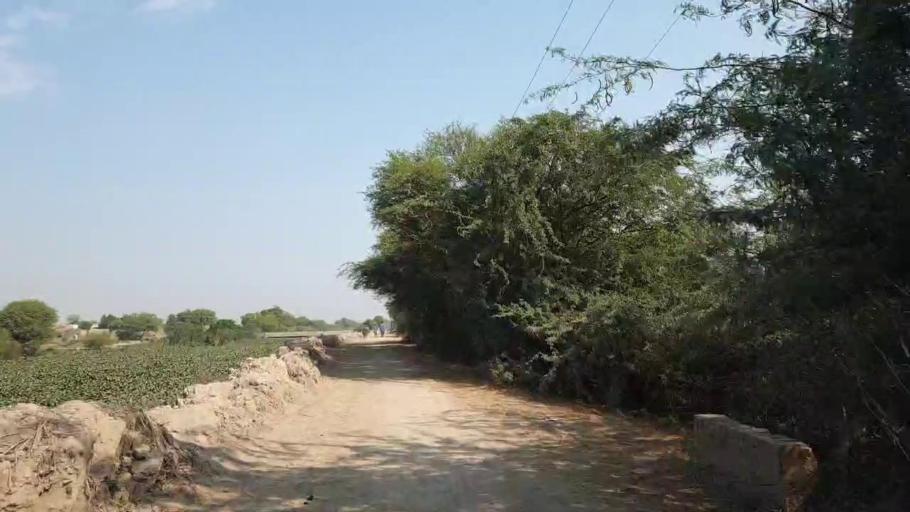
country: PK
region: Sindh
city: Tando Muhammad Khan
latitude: 25.0767
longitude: 68.4197
